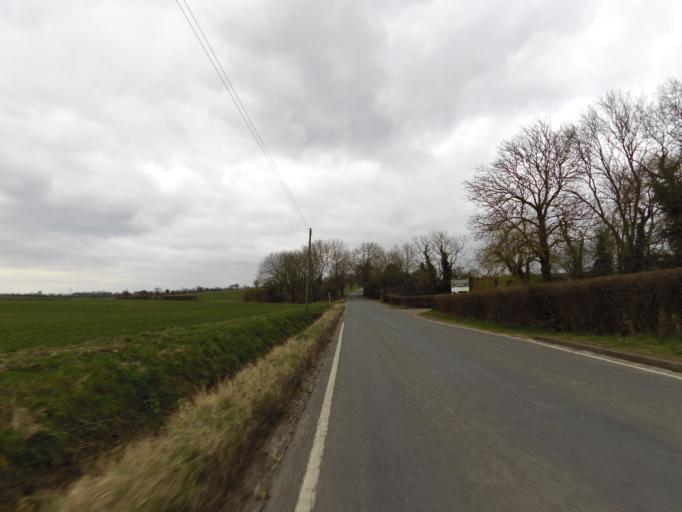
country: GB
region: England
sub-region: Suffolk
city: Ipswich
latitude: 52.1213
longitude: 1.1594
